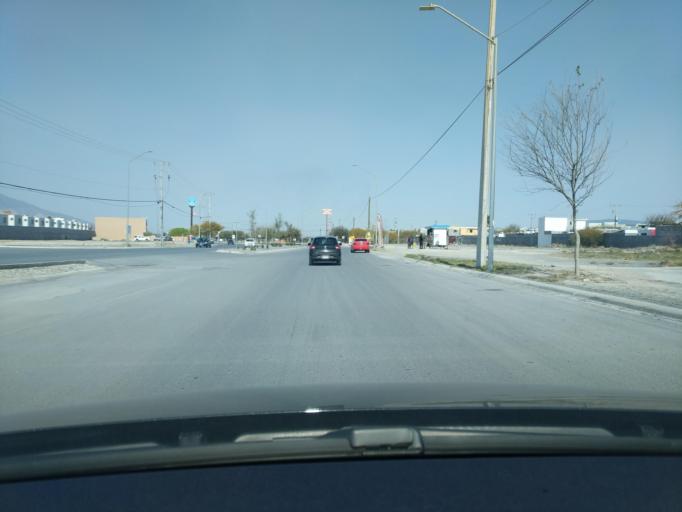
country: MX
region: Nuevo Leon
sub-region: Garcia
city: Los Parques
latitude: 25.7830
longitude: -100.4874
